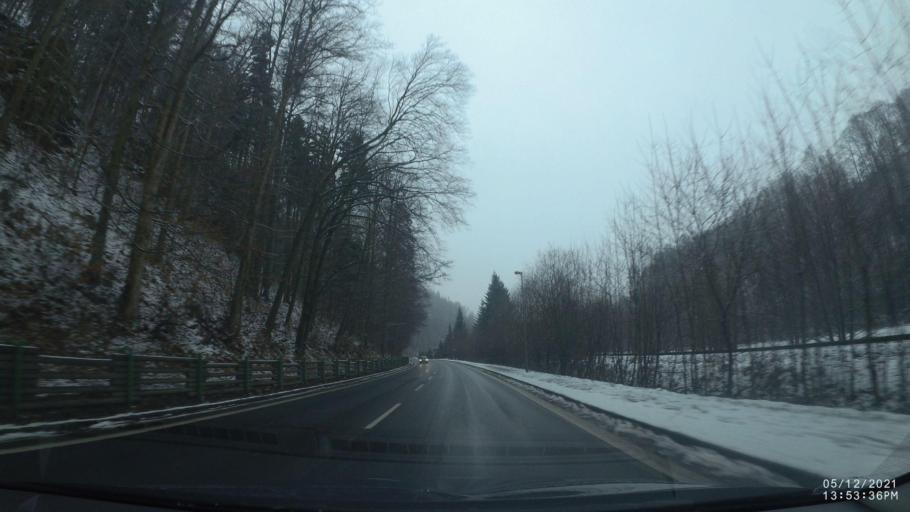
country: CZ
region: Kralovehradecky
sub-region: Okres Nachod
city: Police nad Metuji
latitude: 50.5159
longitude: 16.2118
